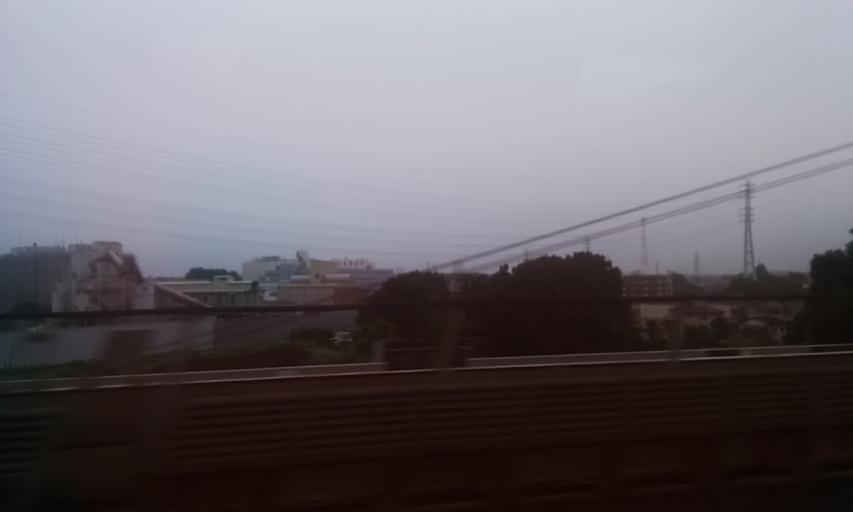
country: JP
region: Saitama
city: Ageoshimo
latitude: 35.9621
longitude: 139.6220
